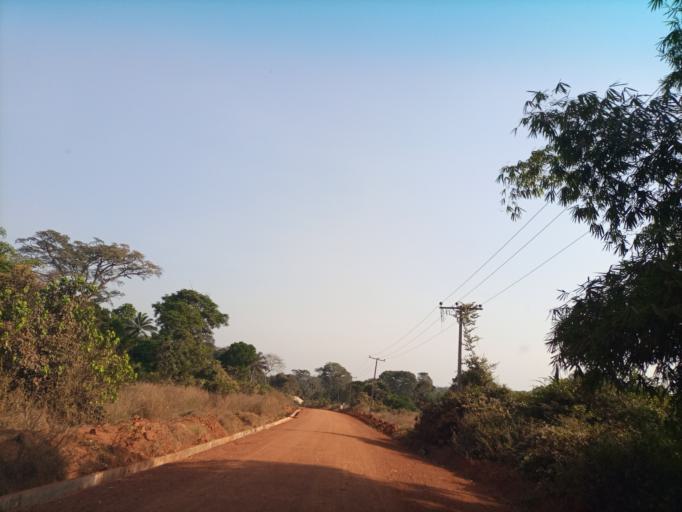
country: NG
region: Enugu
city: Opi
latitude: 6.7623
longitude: 7.3973
